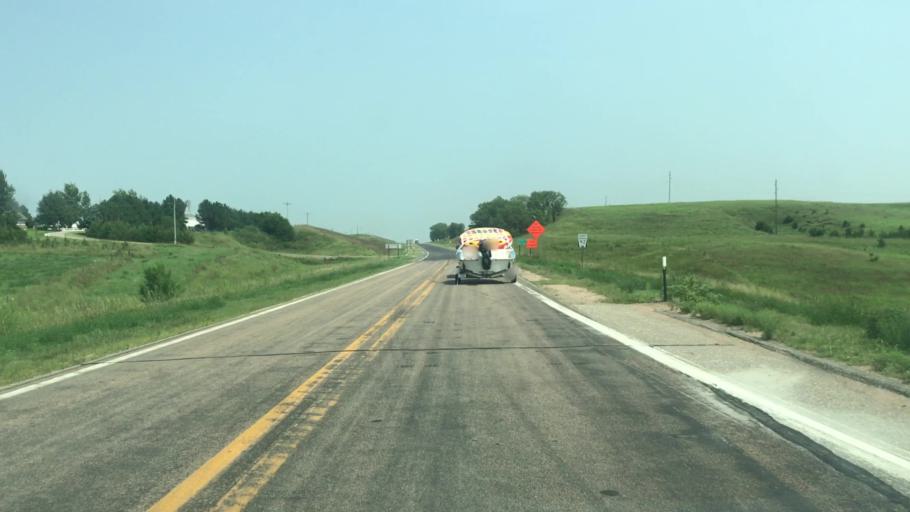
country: US
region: Nebraska
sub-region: Sherman County
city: Loup City
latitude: 41.2628
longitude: -98.9383
